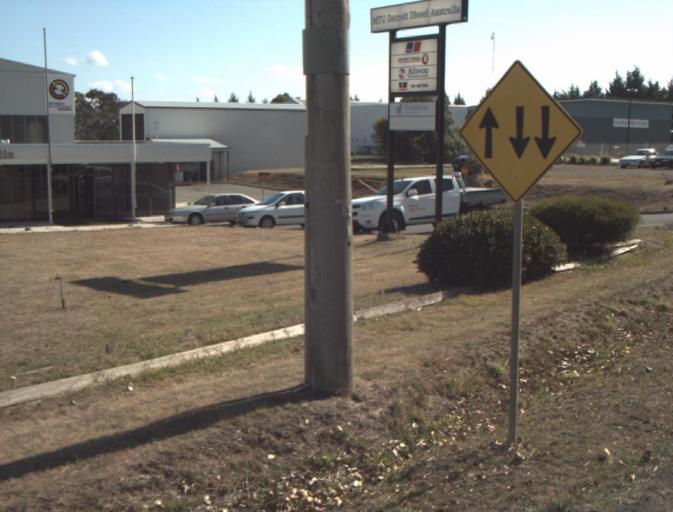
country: AU
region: Tasmania
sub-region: Launceston
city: Mayfield
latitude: -41.3770
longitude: 147.1251
